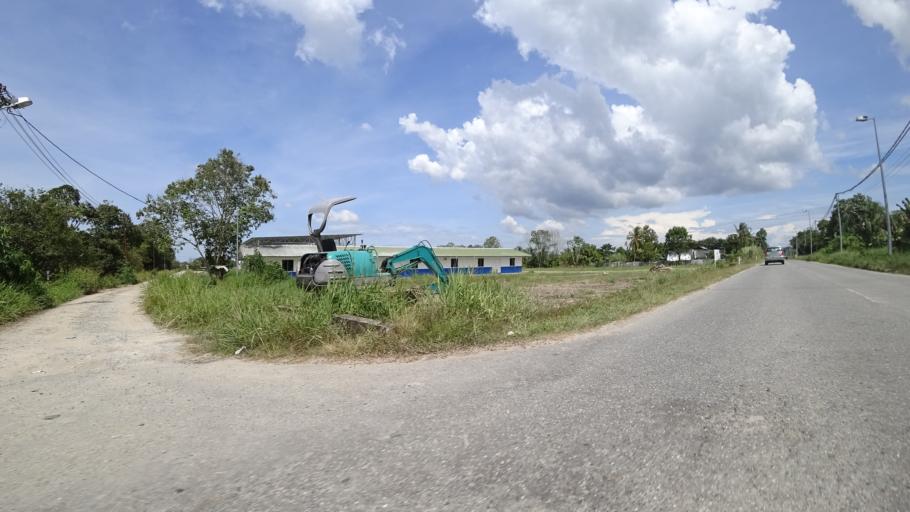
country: BN
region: Brunei and Muara
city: Bandar Seri Begawan
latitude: 4.8433
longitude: 114.8472
